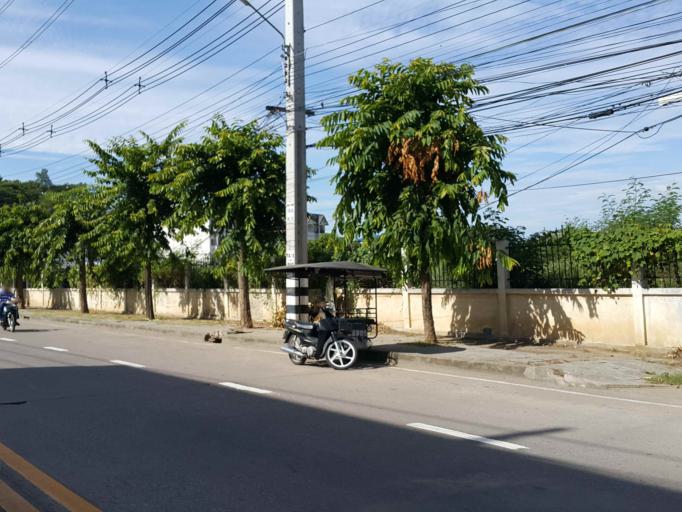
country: TH
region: Chiang Mai
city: Chiang Mai
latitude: 18.7659
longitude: 99.0002
